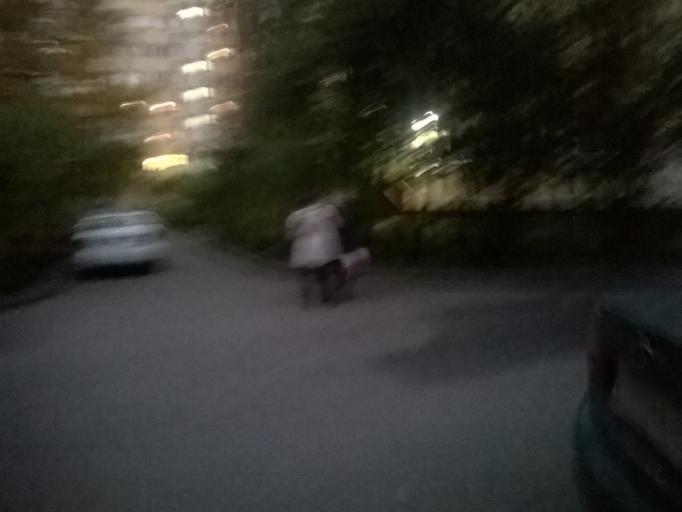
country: RU
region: St.-Petersburg
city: Ozerki
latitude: 60.0339
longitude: 30.3267
